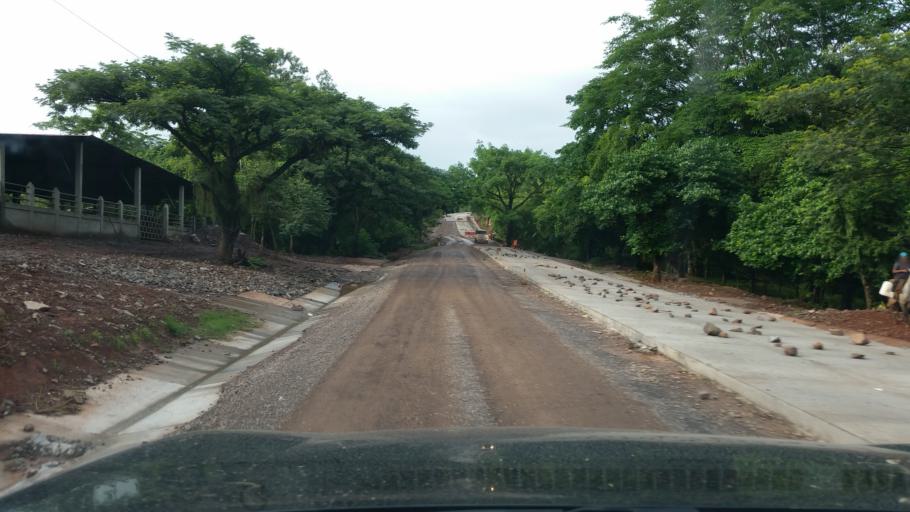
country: NI
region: Matagalpa
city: Rio Blanco
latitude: 13.1163
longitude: -85.0614
